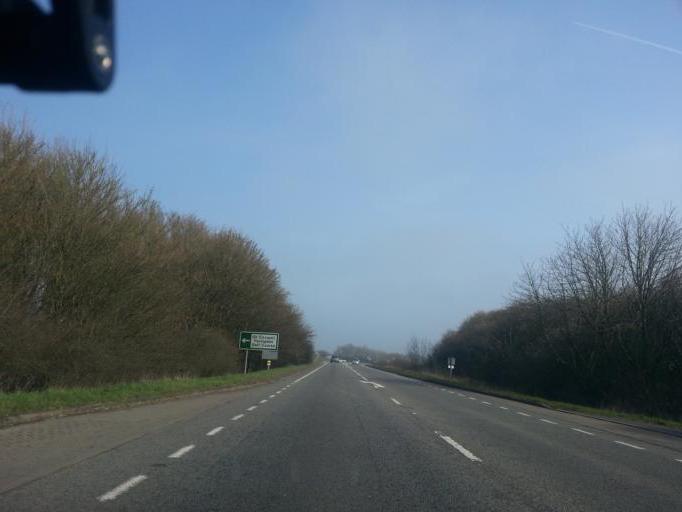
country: GB
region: England
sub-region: Oxfordshire
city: Faringdon
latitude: 51.6405
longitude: -1.6017
